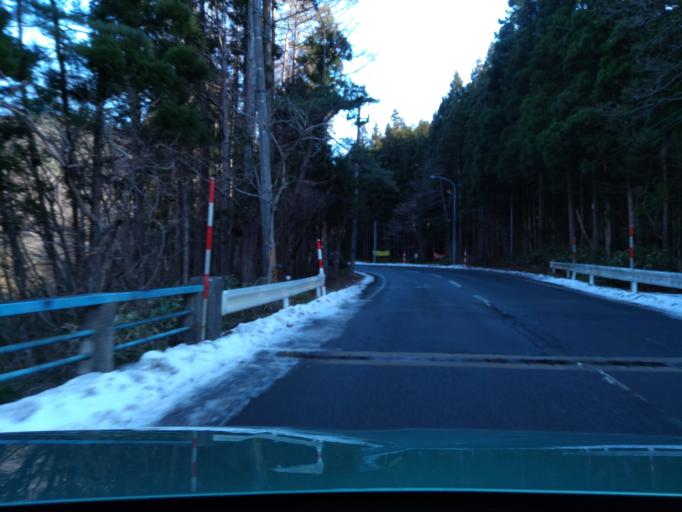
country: JP
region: Iwate
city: Hanamaki
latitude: 39.4389
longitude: 141.0097
